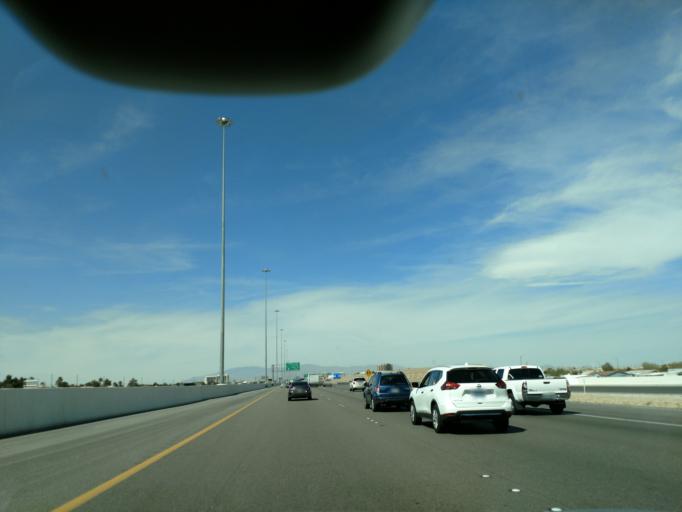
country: US
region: Nevada
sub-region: Clark County
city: Enterprise
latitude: 36.0157
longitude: -115.1804
